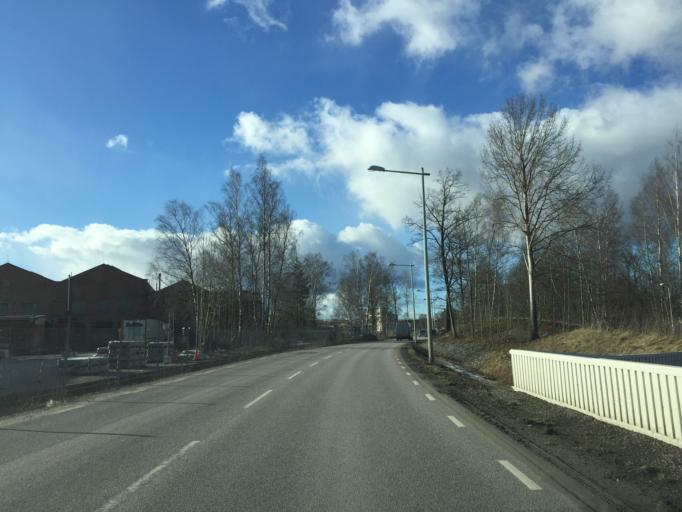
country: SE
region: OErebro
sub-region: Orebro Kommun
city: Orebro
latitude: 59.2780
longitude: 15.2350
